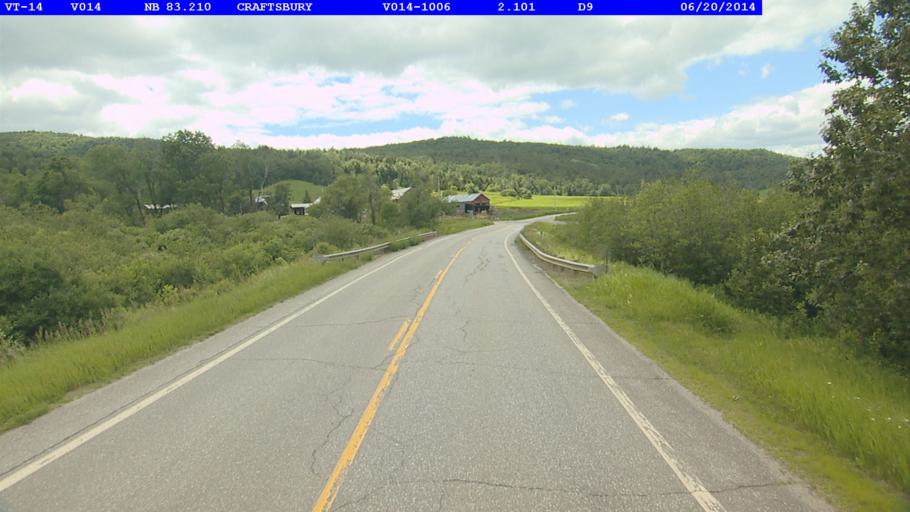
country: US
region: Vermont
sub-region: Caledonia County
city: Hardwick
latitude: 44.6263
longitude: -72.3845
